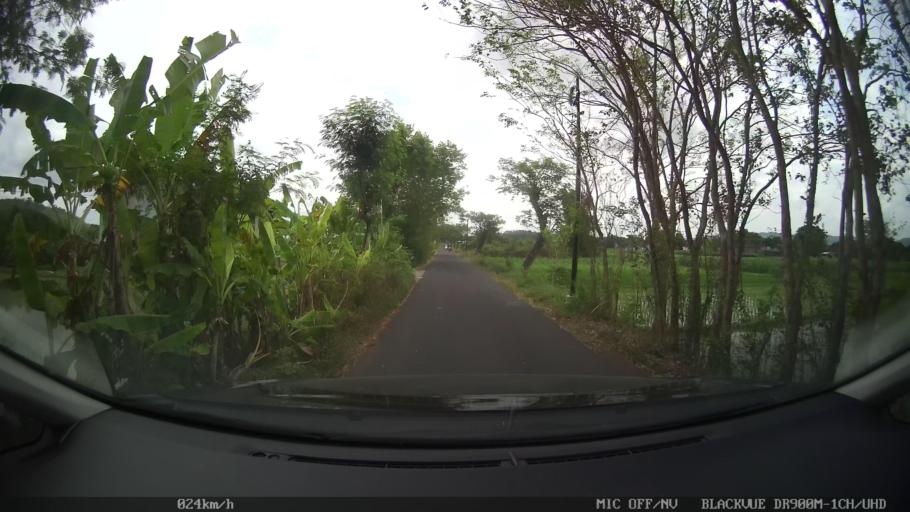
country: ID
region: Daerah Istimewa Yogyakarta
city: Depok
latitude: -7.8252
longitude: 110.4639
